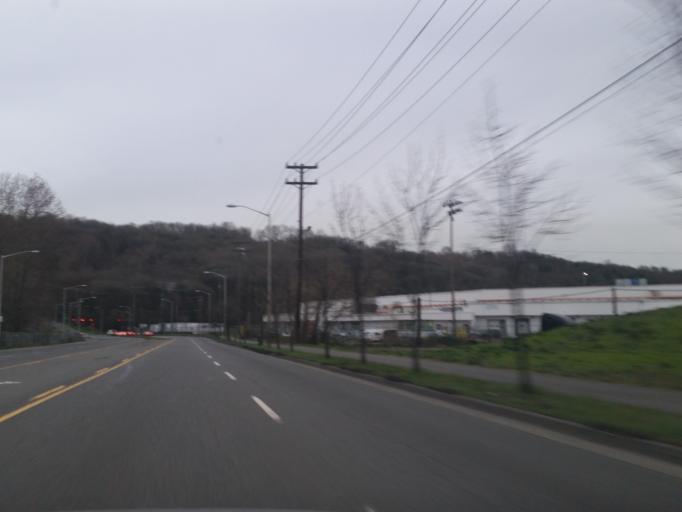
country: US
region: Washington
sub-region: King County
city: White Center
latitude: 47.5400
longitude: -122.3383
